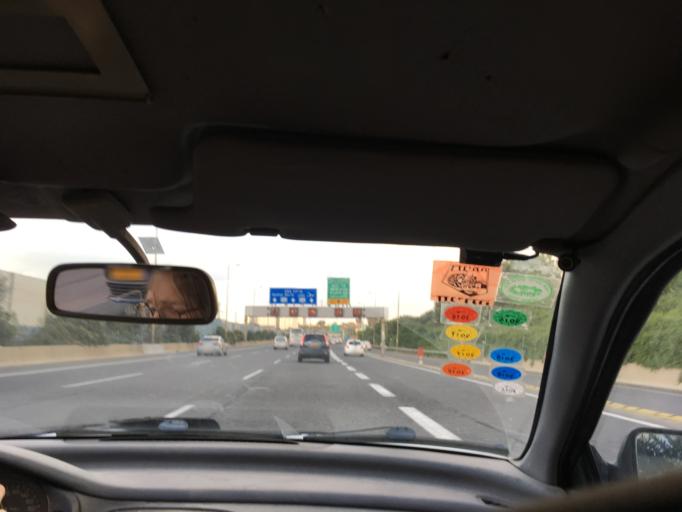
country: IL
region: Tel Aviv
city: Ramat Gan
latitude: 32.0940
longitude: 34.8019
